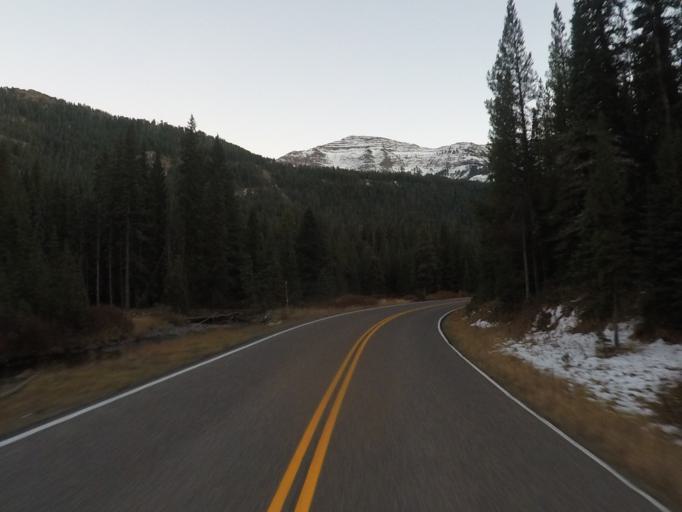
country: US
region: Montana
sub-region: Stillwater County
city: Absarokee
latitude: 44.9397
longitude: -110.0836
